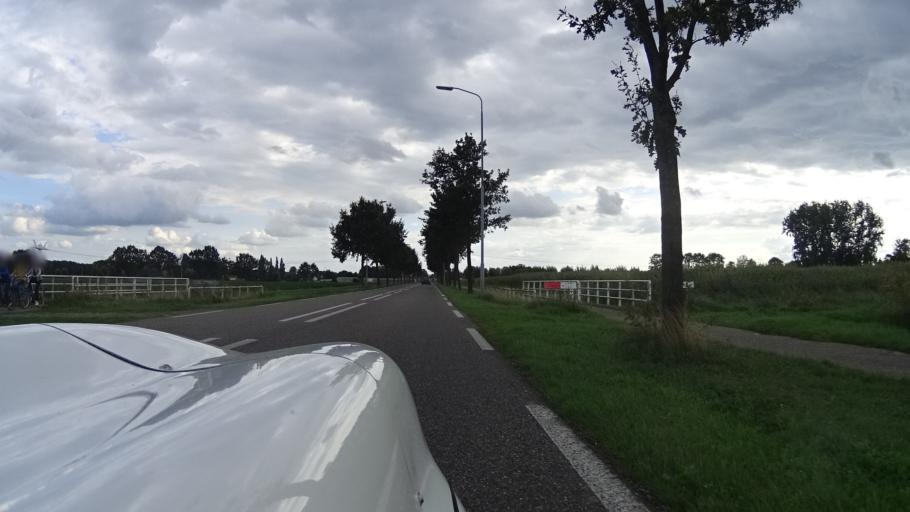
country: NL
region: North Brabant
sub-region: Gemeente Heusden
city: Heusden
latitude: 51.7147
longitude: 5.1821
